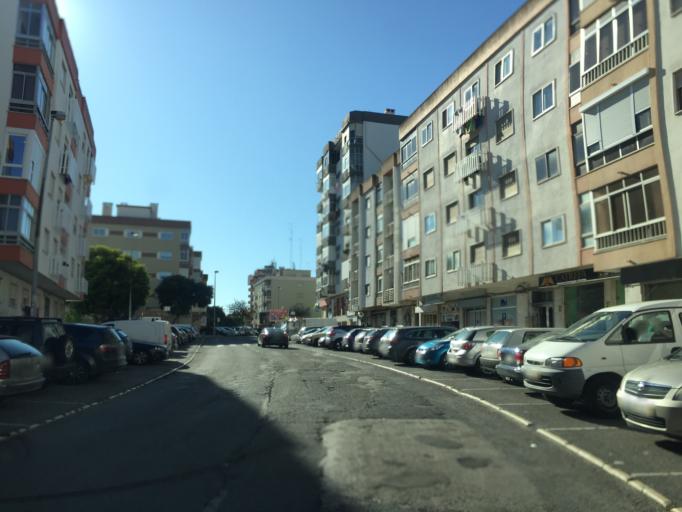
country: PT
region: Lisbon
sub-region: Sintra
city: Queluz
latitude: 38.7598
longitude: -9.2504
